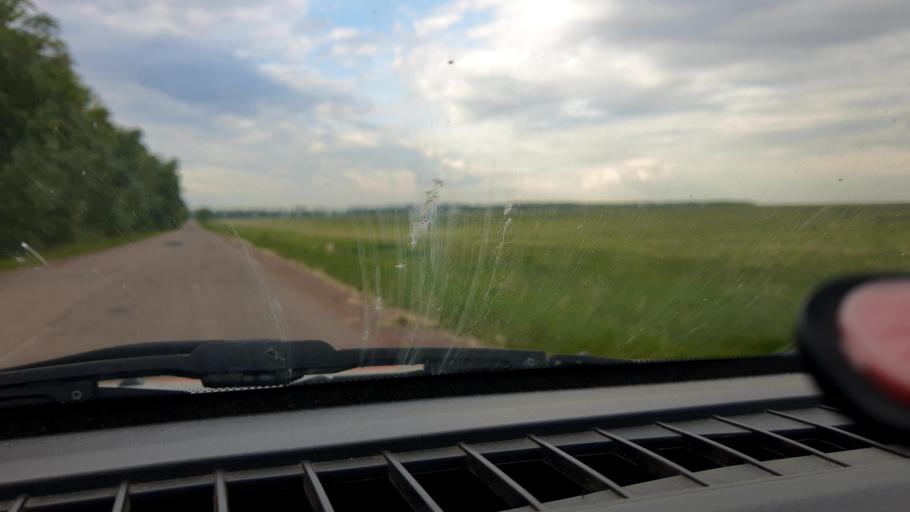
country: RU
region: Bashkortostan
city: Asanovo
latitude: 54.8209
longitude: 55.5950
